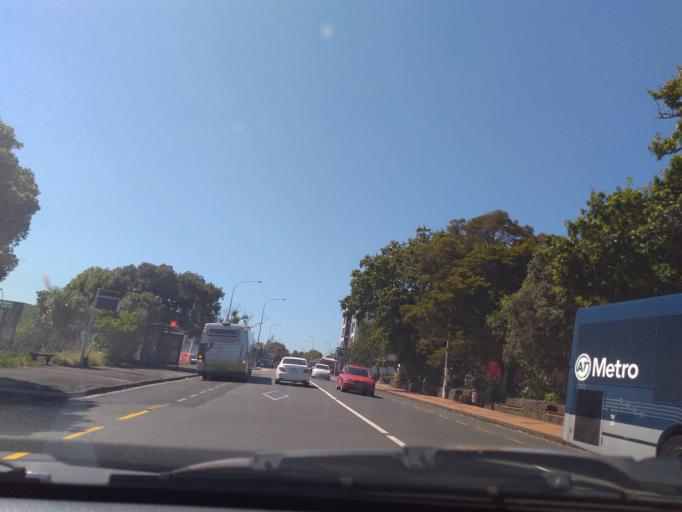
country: NZ
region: Auckland
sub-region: Auckland
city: Rosebank
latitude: -36.8963
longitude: 174.6972
